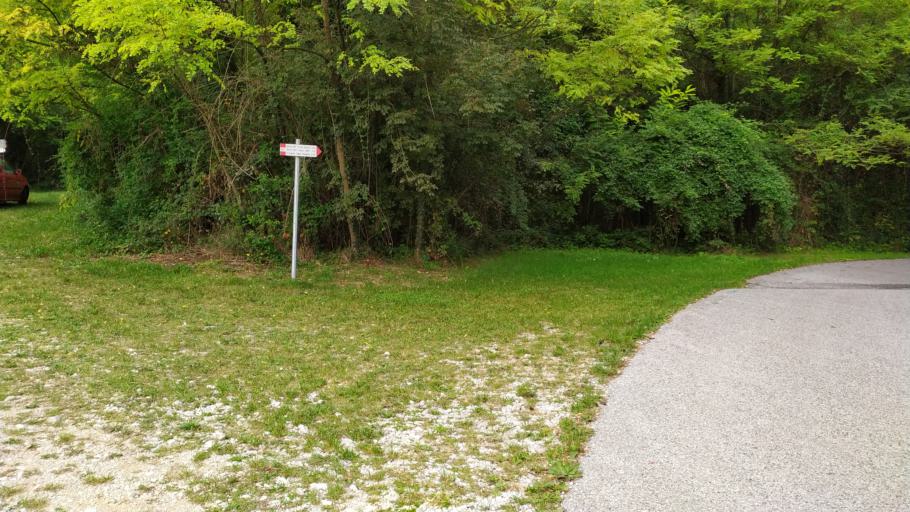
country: IT
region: Friuli Venezia Giulia
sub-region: Provincia di Pordenone
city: Marsure
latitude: 46.0895
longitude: 12.5726
